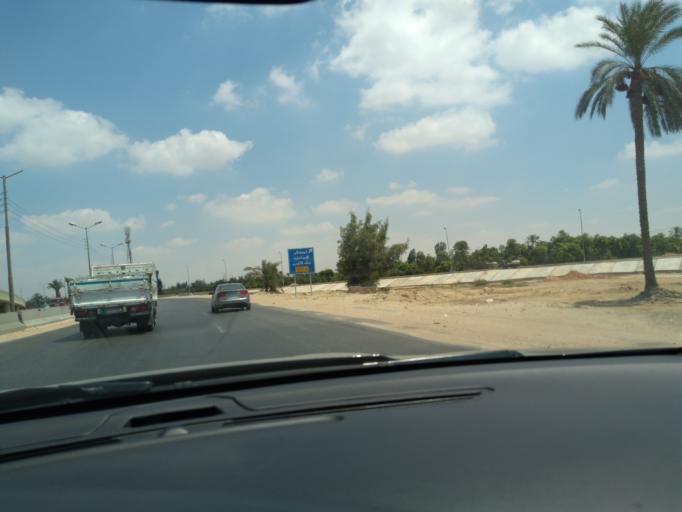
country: EG
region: Al Isma'iliyah
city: Ismailia
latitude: 30.6671
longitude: 32.2712
